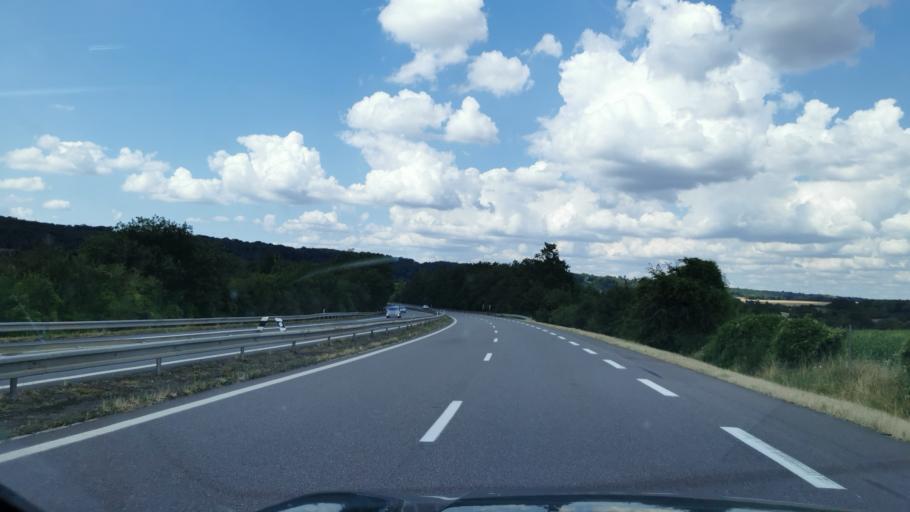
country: FR
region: Lorraine
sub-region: Departement de Meurthe-et-Moselle
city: Crusnes
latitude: 49.4178
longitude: 5.9181
